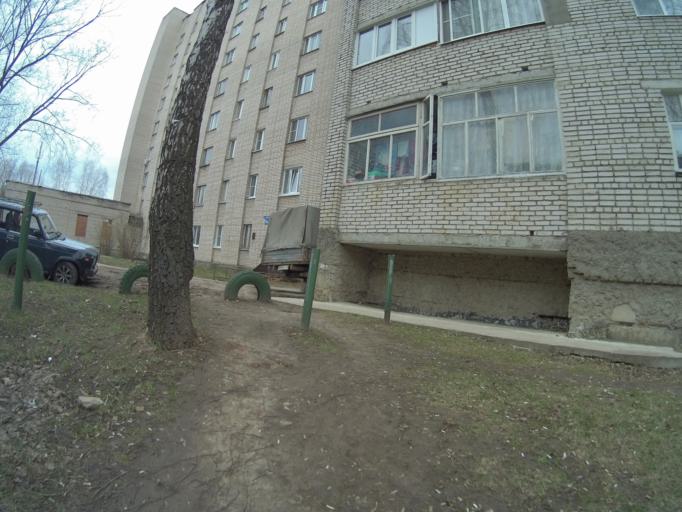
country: RU
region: Vladimir
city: Vladimir
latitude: 56.1480
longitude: 40.4214
